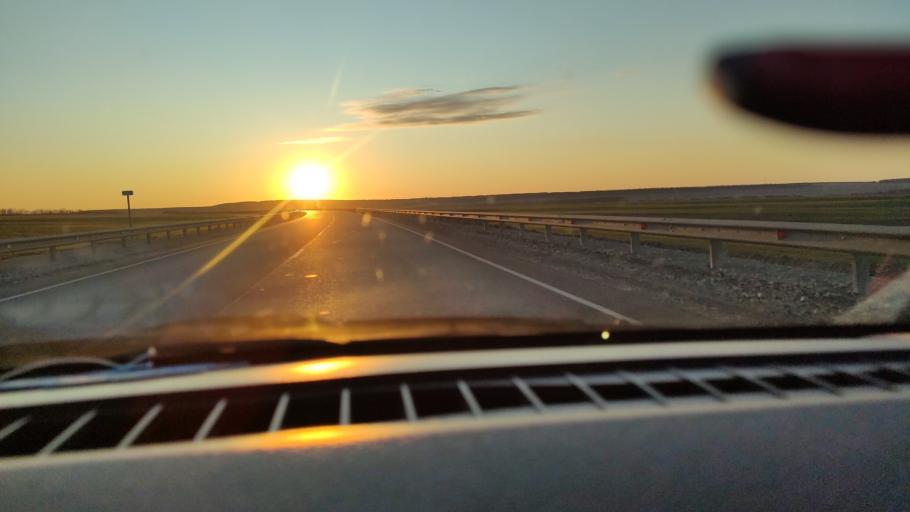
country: RU
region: Saratov
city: Yelshanka
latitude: 51.8319
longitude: 46.4579
